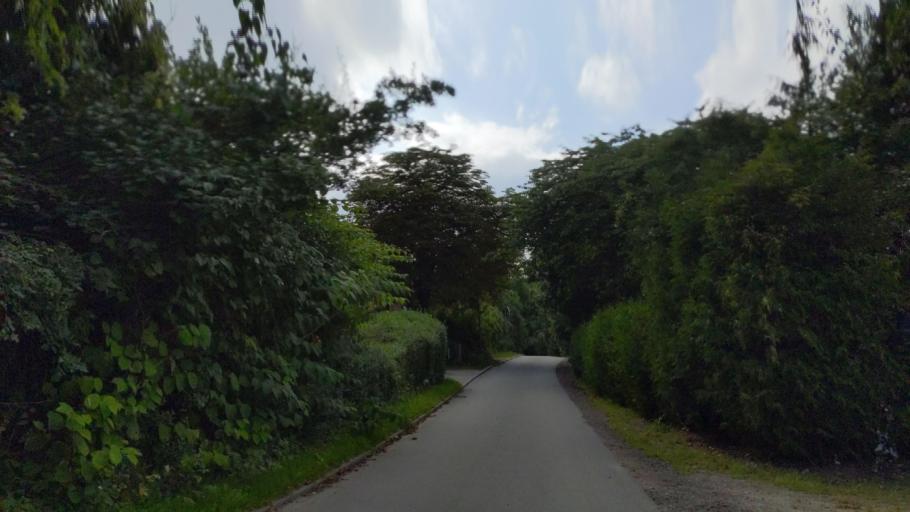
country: DE
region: Schleswig-Holstein
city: Kirchnuchel
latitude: 54.1590
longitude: 10.6591
